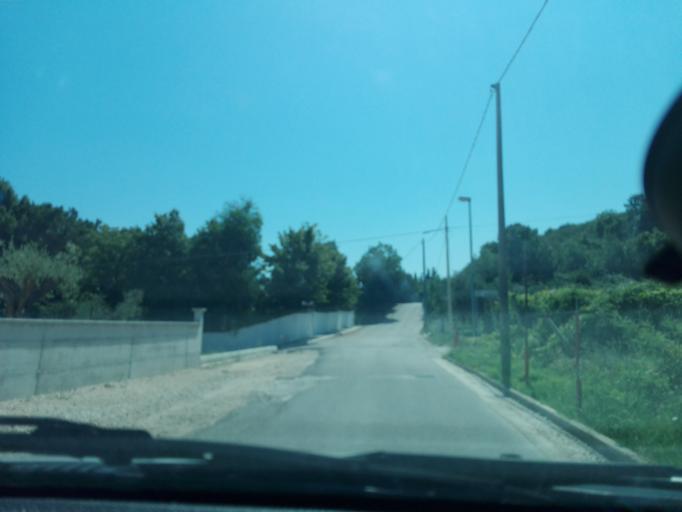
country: IT
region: Abruzzo
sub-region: Provincia di Pescara
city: Montesilvano Marina
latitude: 42.5002
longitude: 14.1576
